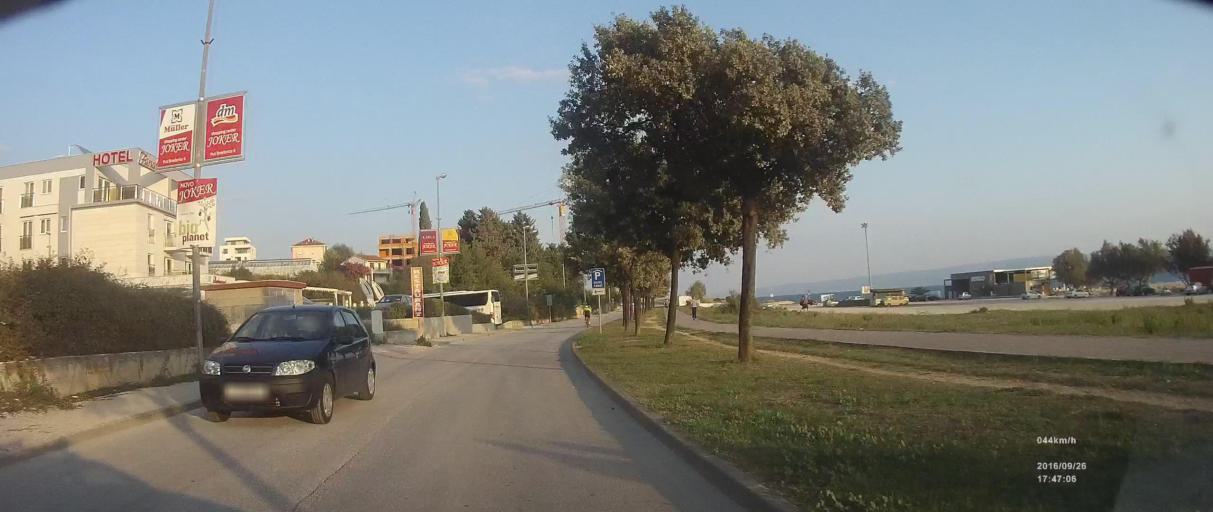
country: HR
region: Splitsko-Dalmatinska
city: Vranjic
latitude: 43.5032
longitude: 16.4796
